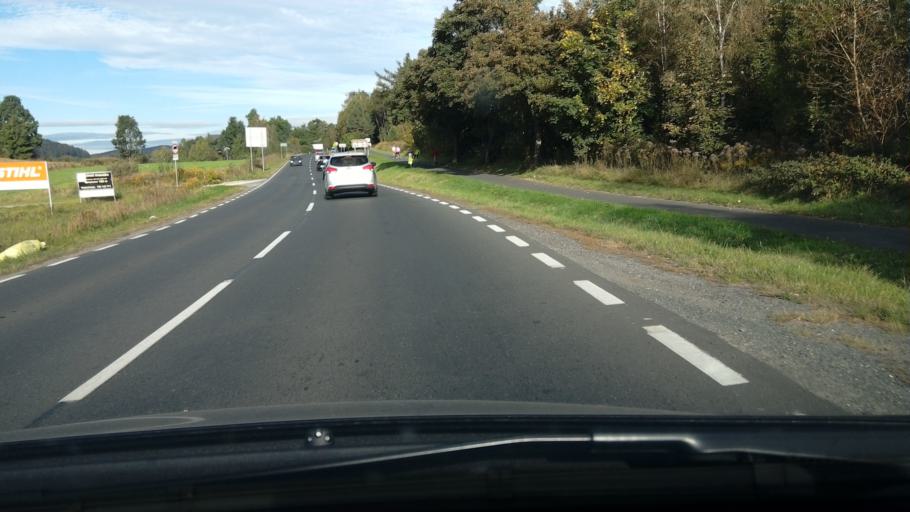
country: PL
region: Lower Silesian Voivodeship
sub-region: Powiat jeleniogorski
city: Myslakowice
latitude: 50.8703
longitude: 15.7652
